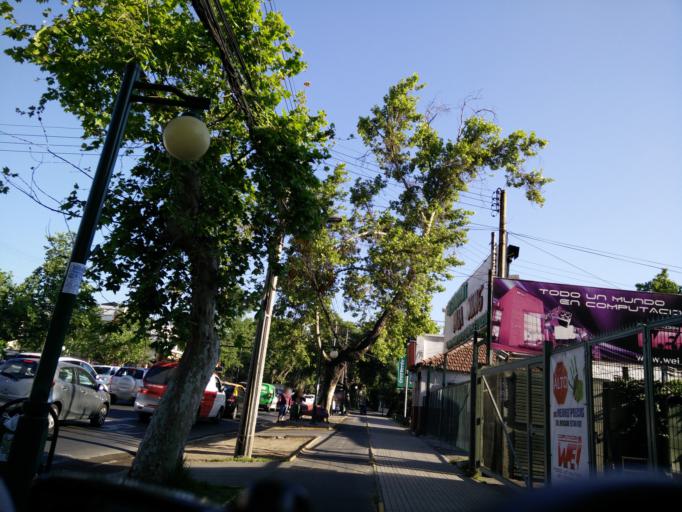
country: CL
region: Santiago Metropolitan
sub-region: Provincia de Santiago
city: Villa Presidente Frei, Nunoa, Santiago, Chile
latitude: -33.4460
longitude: -70.6059
